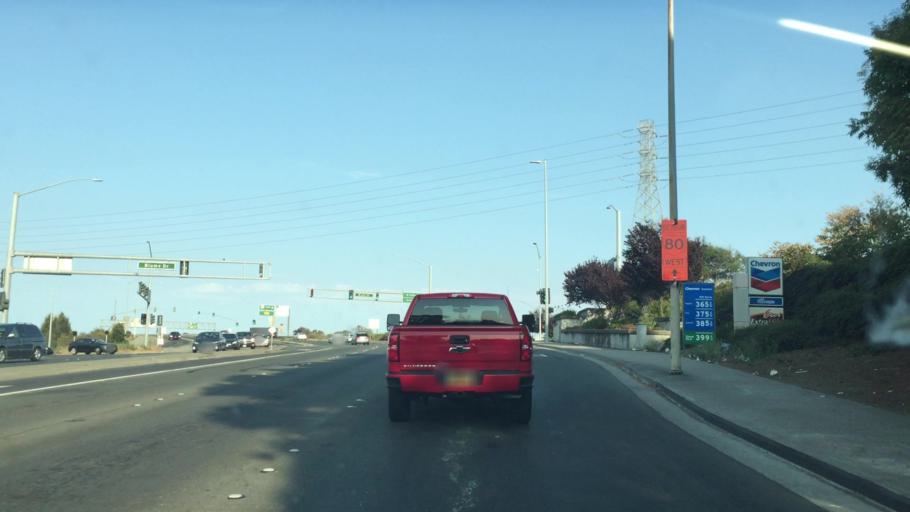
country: US
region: California
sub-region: Contra Costa County
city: Tara Hills
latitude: 37.9872
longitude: -122.3181
